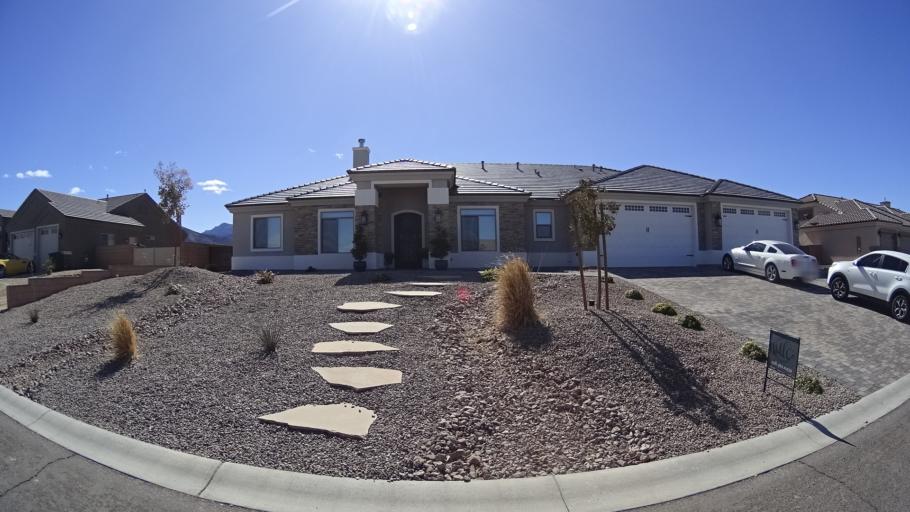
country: US
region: Arizona
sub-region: Mohave County
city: Kingman
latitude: 35.1966
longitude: -113.9698
